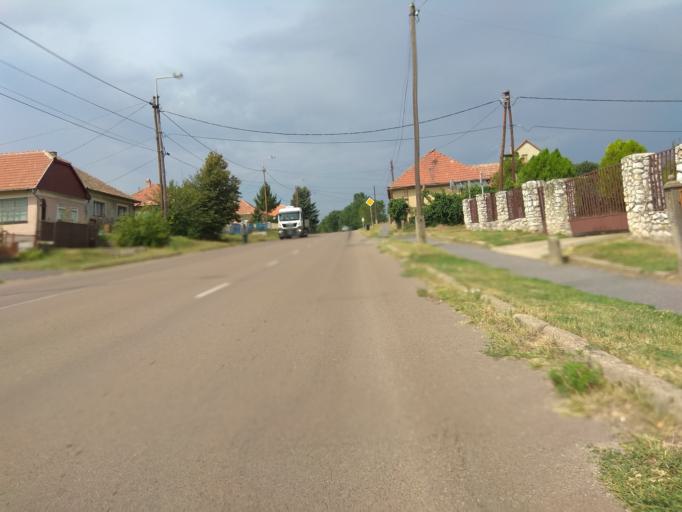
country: HU
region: Borsod-Abauj-Zemplen
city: Emod
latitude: 47.9311
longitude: 20.8096
